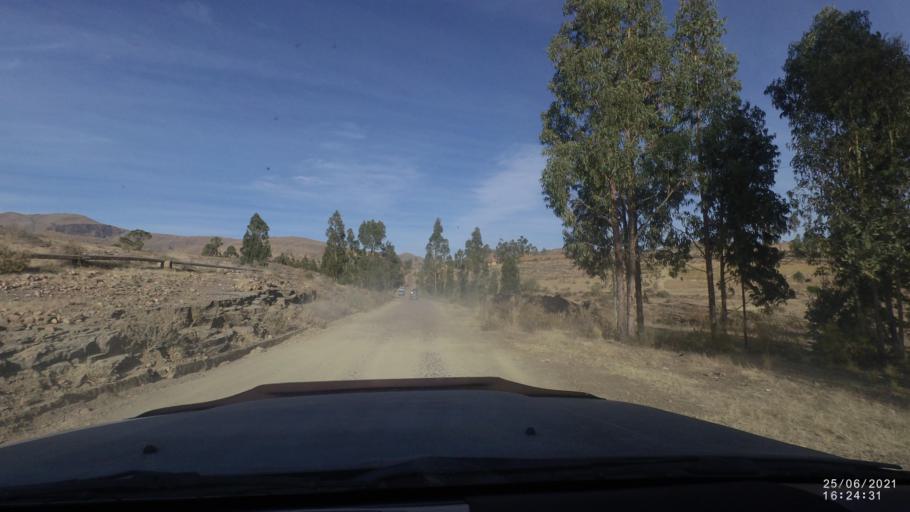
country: BO
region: Cochabamba
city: Arani
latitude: -17.7644
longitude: -65.8253
